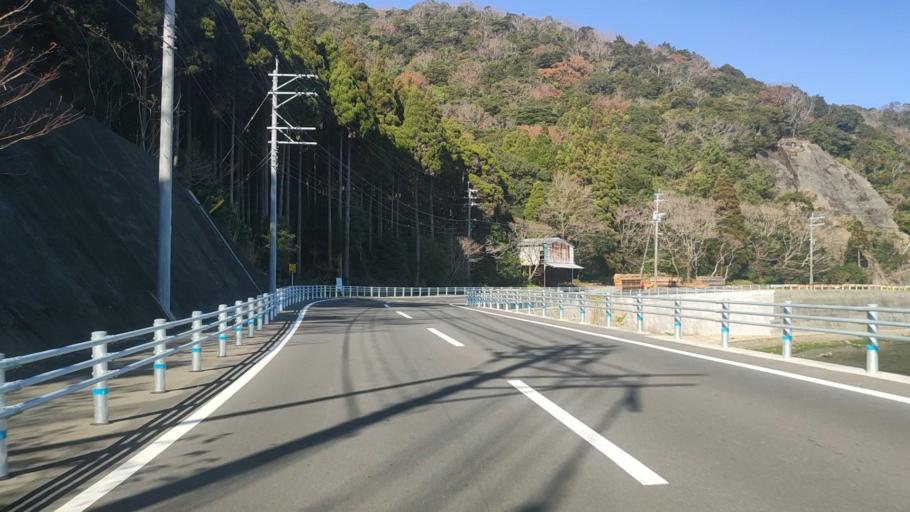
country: JP
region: Oita
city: Saiki
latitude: 32.7958
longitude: 131.8870
